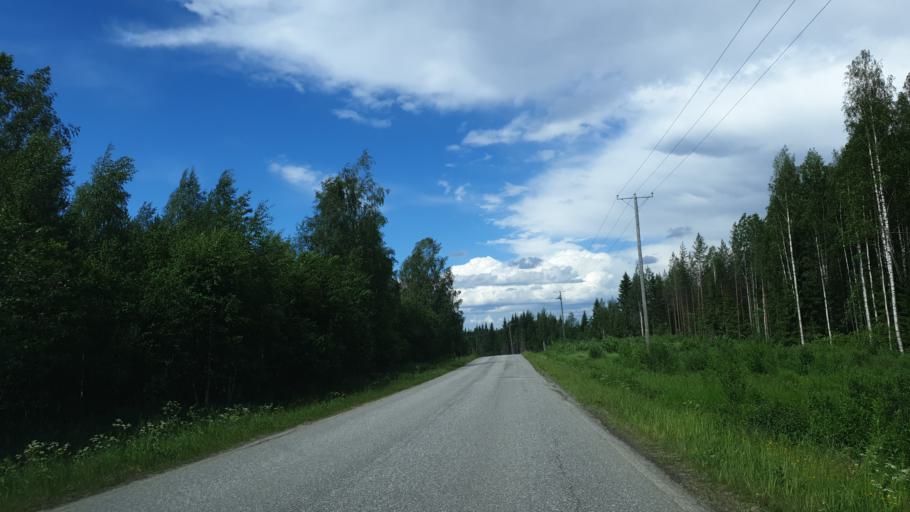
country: FI
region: Northern Savo
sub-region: Koillis-Savo
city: Kaavi
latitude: 62.9791
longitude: 28.7461
